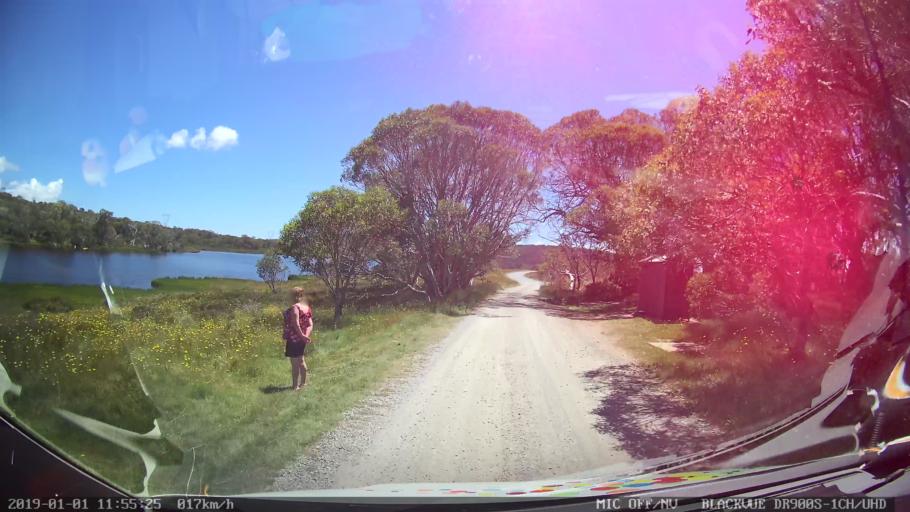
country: AU
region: New South Wales
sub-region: Snowy River
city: Jindabyne
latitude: -35.8884
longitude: 148.4485
